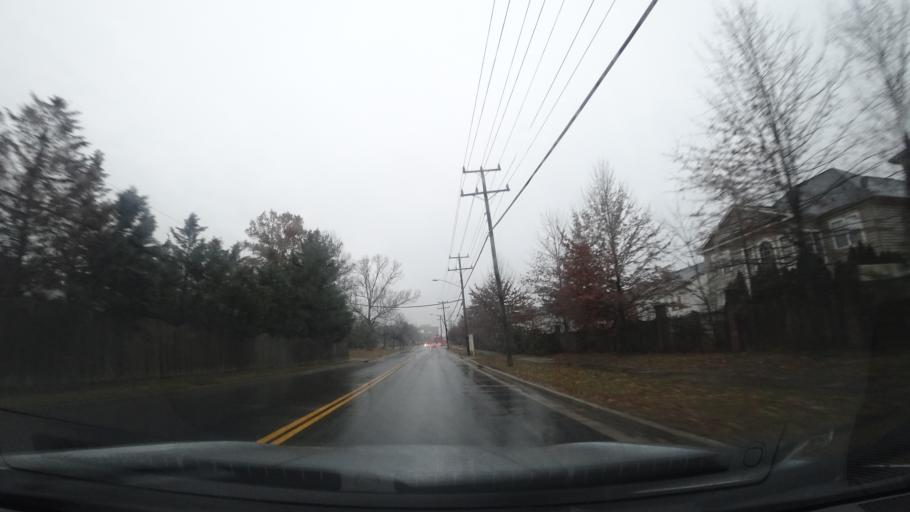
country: US
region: Virginia
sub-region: Fairfax County
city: Herndon
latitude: 38.9597
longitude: -77.3866
